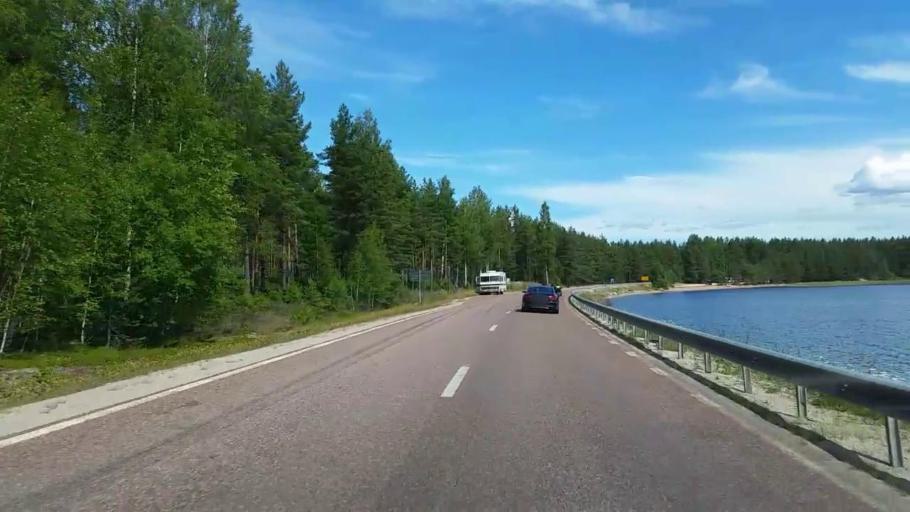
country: SE
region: Dalarna
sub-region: Rattviks Kommun
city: Raettvik
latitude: 61.1721
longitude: 15.1531
